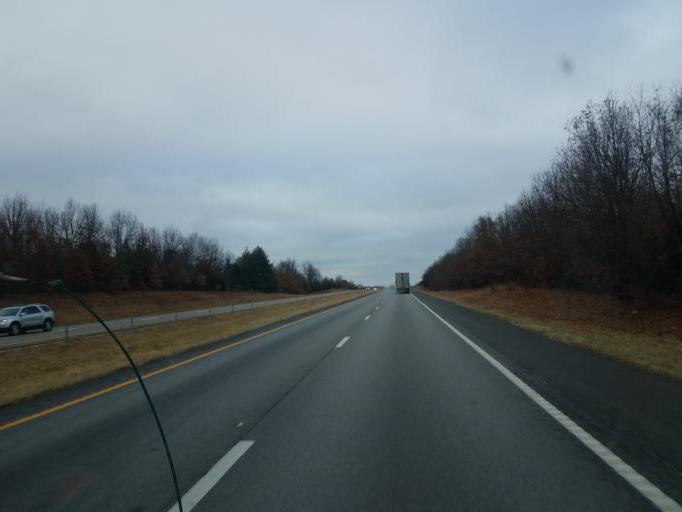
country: US
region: Missouri
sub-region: Webster County
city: Marshfield
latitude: 37.4894
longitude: -92.8495
